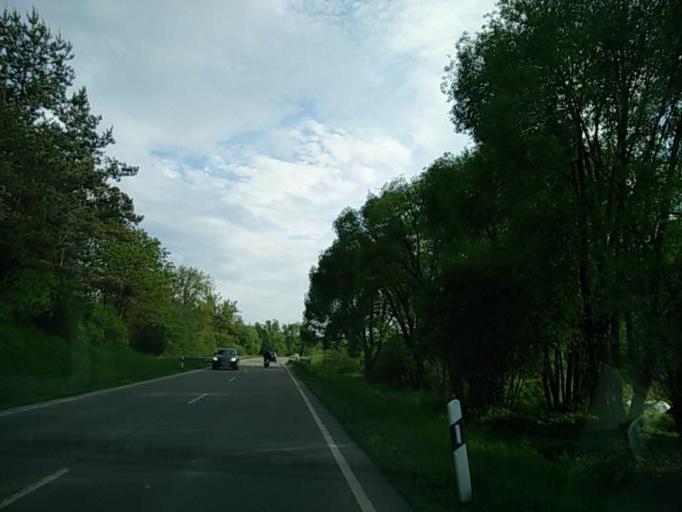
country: DE
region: Baden-Wuerttemberg
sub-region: Tuebingen Region
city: Hirrlingen
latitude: 48.4330
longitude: 8.9187
